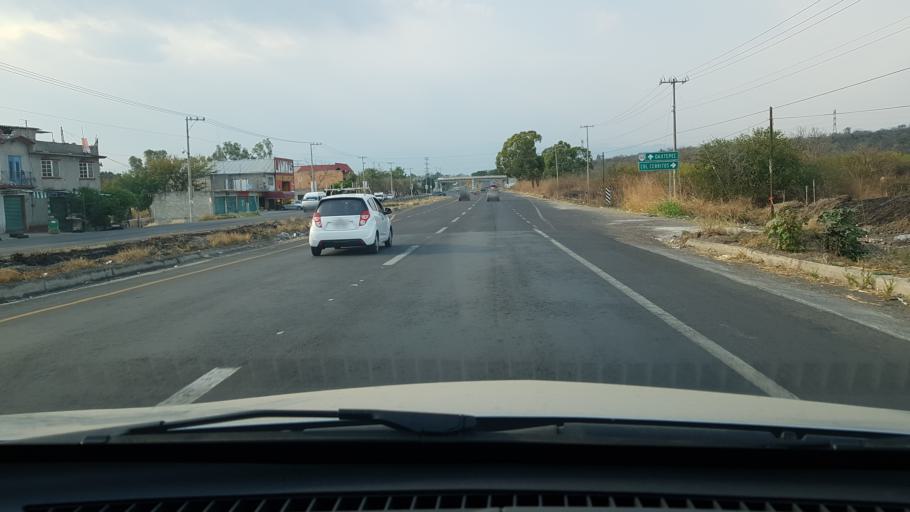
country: MX
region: Morelos
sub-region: Yecapixtla
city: Juan Morales
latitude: 18.8329
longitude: -98.9226
